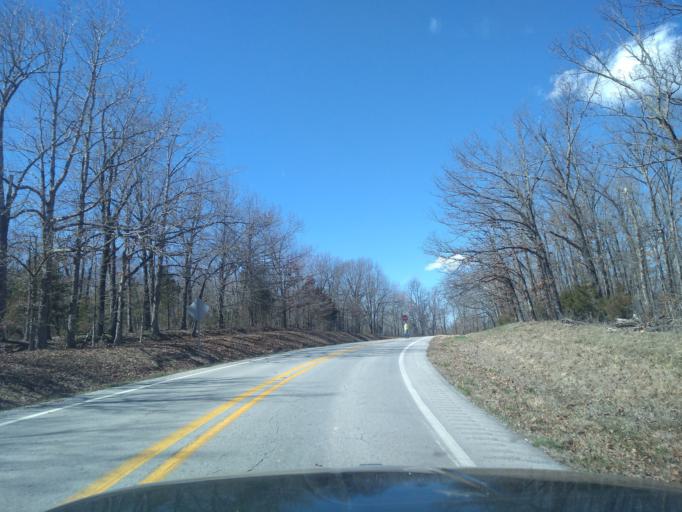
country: US
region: Arkansas
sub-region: Washington County
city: Farmington
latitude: 36.0843
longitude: -94.3249
